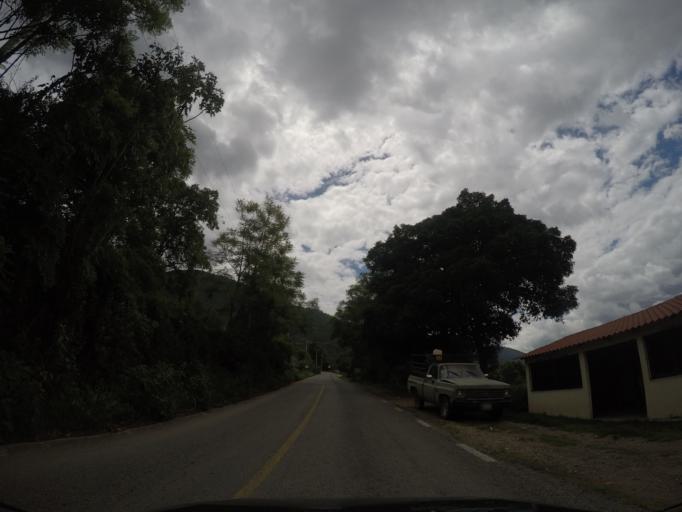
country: MX
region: Oaxaca
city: San Francisco Sola
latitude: 16.4916
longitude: -96.9834
